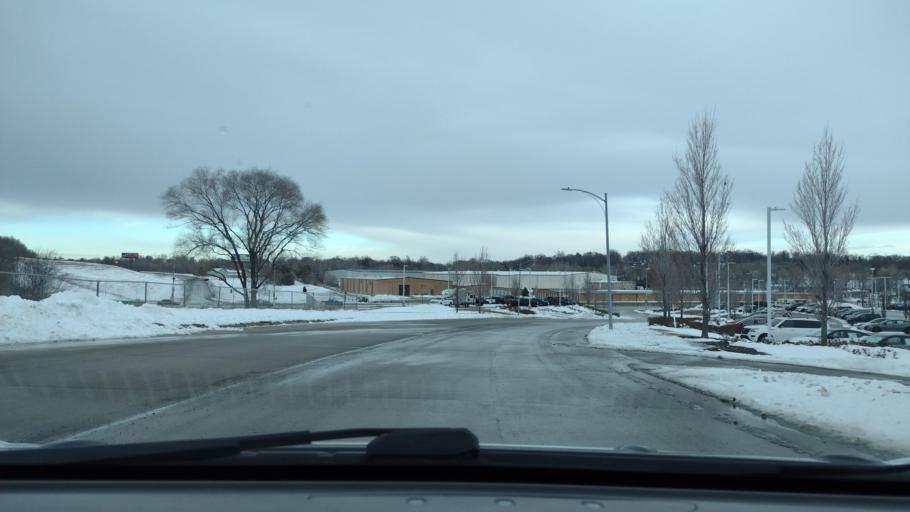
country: US
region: Nebraska
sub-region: Sarpy County
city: Offutt Air Force Base
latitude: 41.1821
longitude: -95.9372
